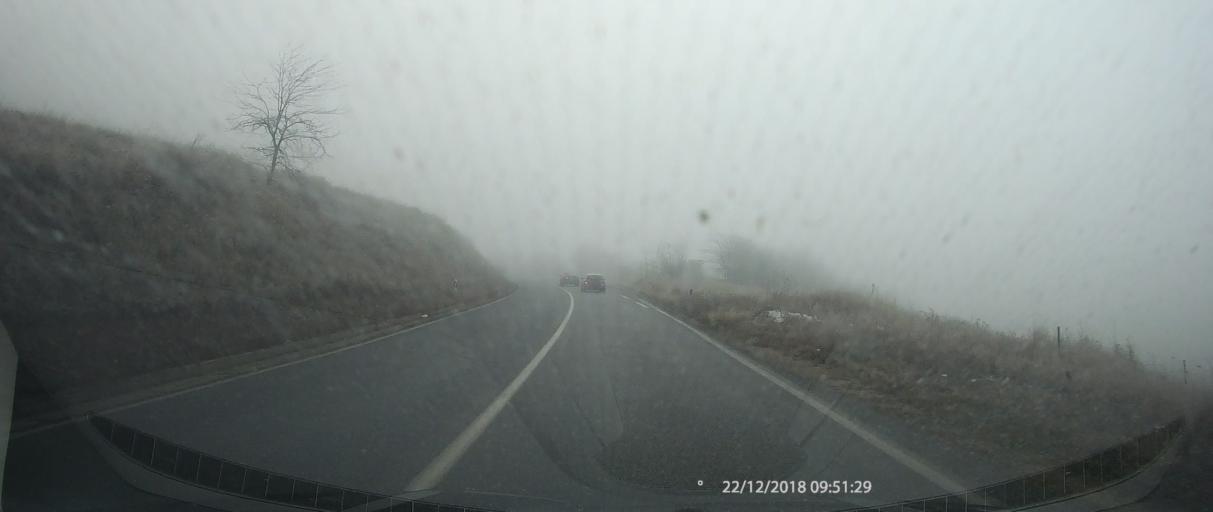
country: MK
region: Staro Nagoricane
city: Staro Nagorichane
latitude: 42.1702
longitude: 21.8062
